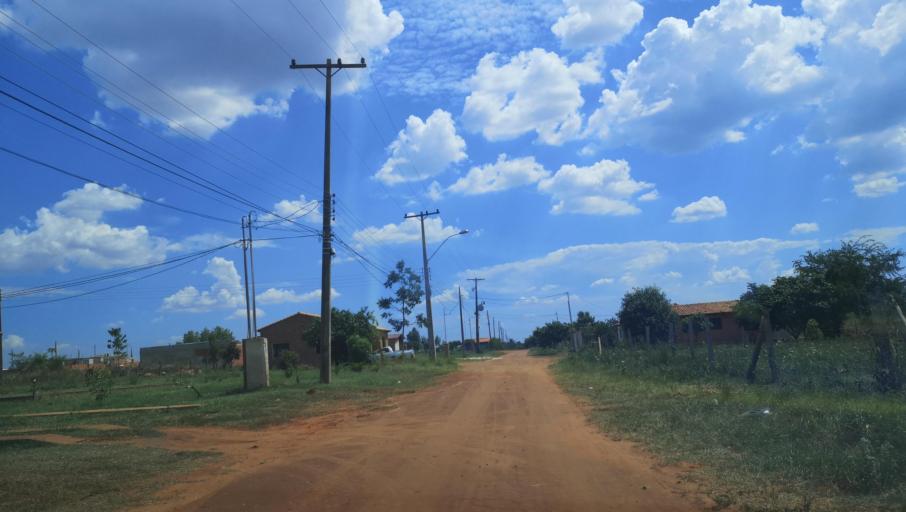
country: PY
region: Misiones
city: Santa Maria
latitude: -26.8910
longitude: -57.0355
